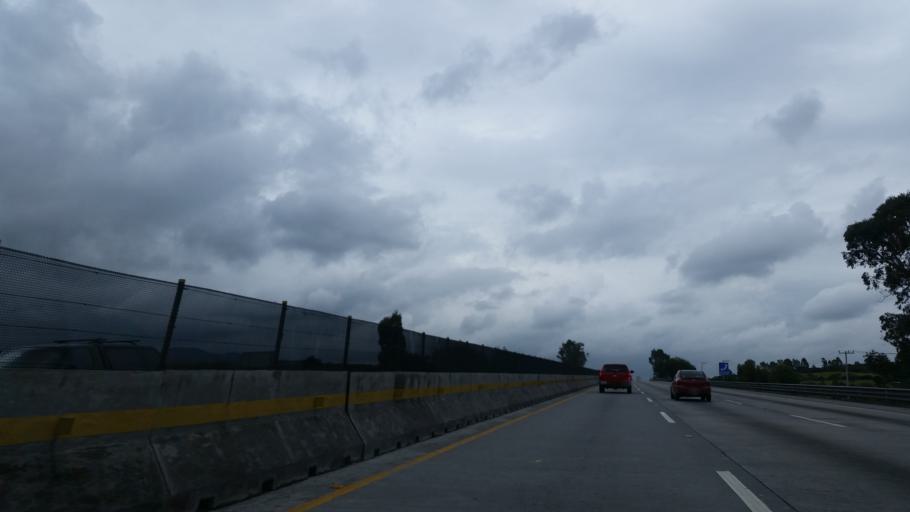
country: MX
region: Hidalgo
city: Tepeji de Ocampo
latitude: 19.9238
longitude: -99.3731
